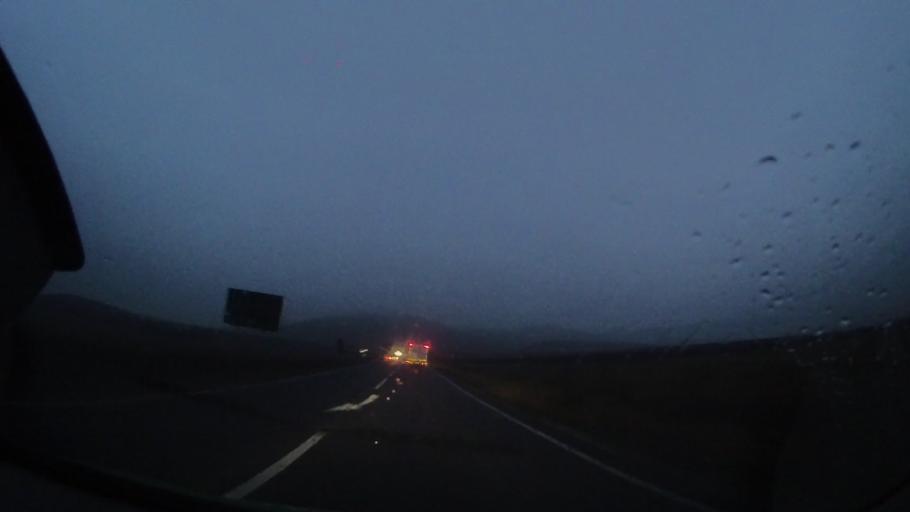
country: RO
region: Harghita
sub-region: Comuna Ditrau
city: Ditrau
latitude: 46.8332
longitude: 25.4918
